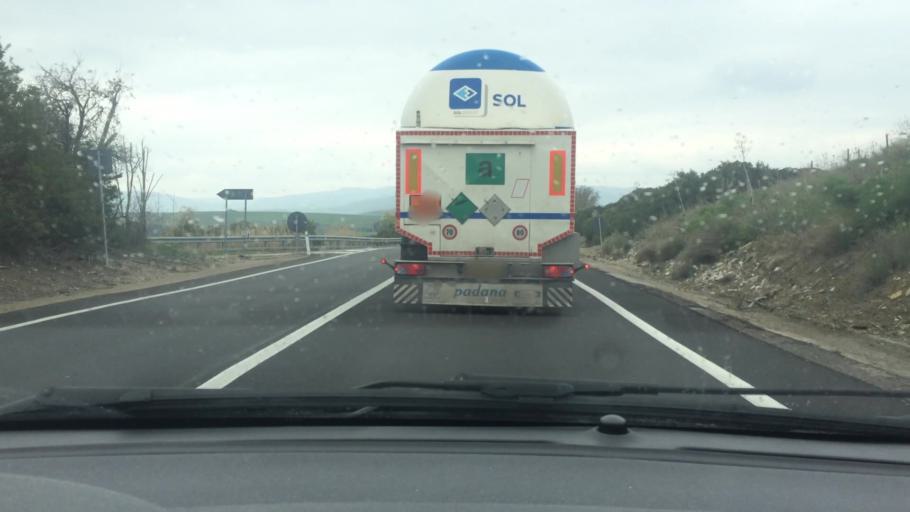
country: IT
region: Basilicate
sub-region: Provincia di Matera
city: Matera
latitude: 40.6212
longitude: 16.5841
